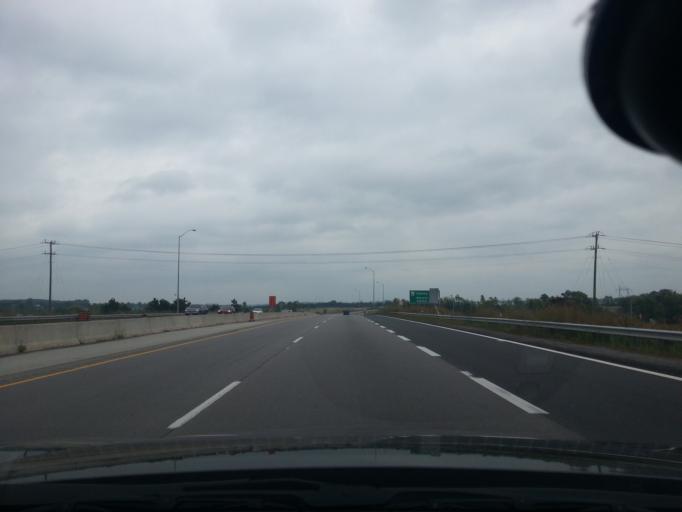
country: CA
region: Ontario
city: Greater Napanee
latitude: 44.2640
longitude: -76.9669
